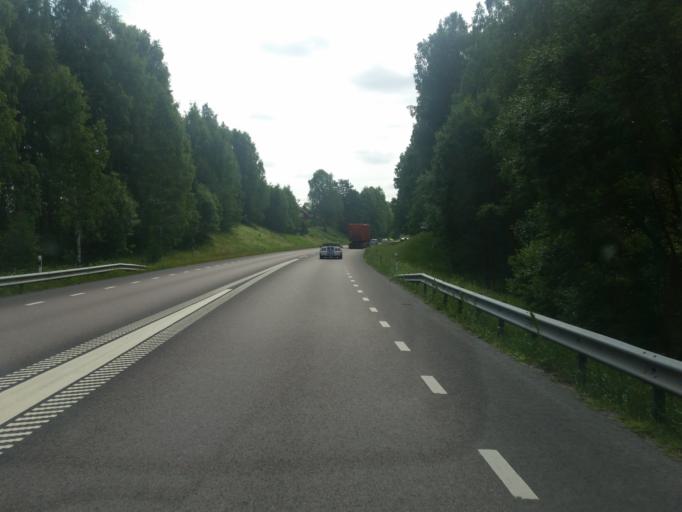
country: SE
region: Dalarna
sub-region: Gagnefs Kommun
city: Gagnef
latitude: 60.5999
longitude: 15.0698
